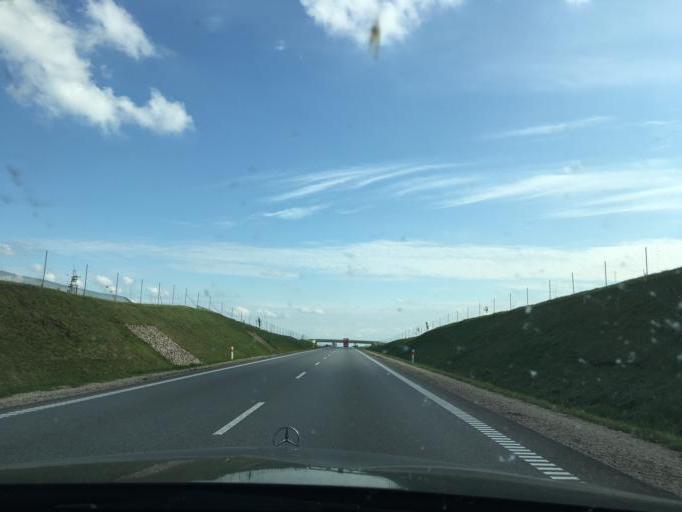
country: PL
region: Podlasie
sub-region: Powiat suwalski
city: Raczki
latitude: 53.9059
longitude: 22.8456
